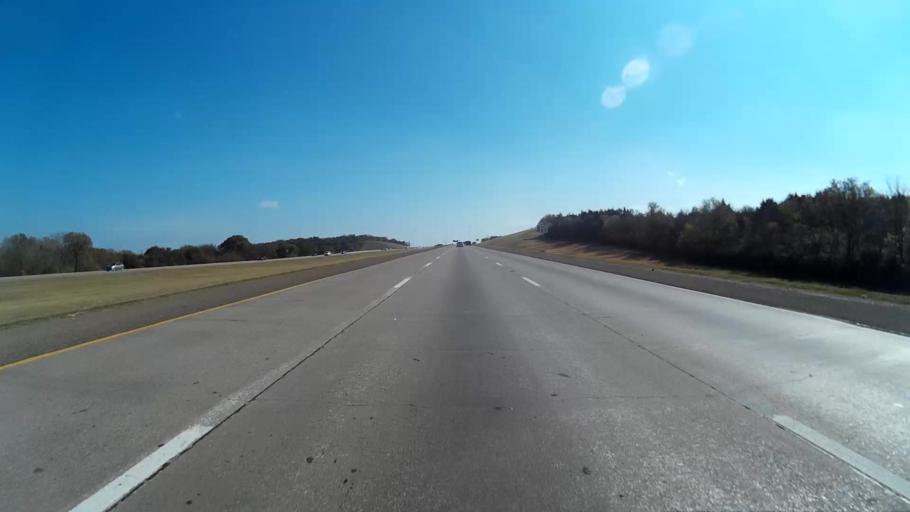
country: US
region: Texas
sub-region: Dallas County
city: Hutchins
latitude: 32.6731
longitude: -96.7371
